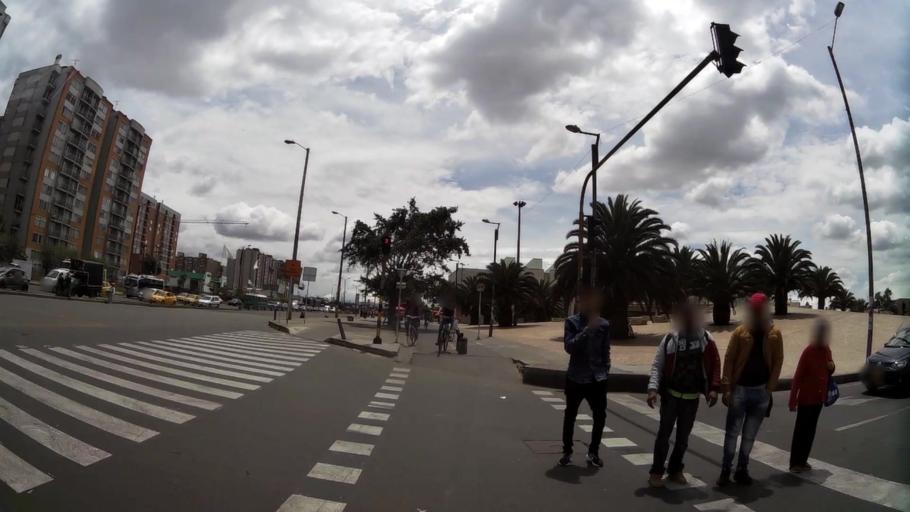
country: CO
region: Bogota D.C.
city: Bogota
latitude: 4.6434
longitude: -74.1535
